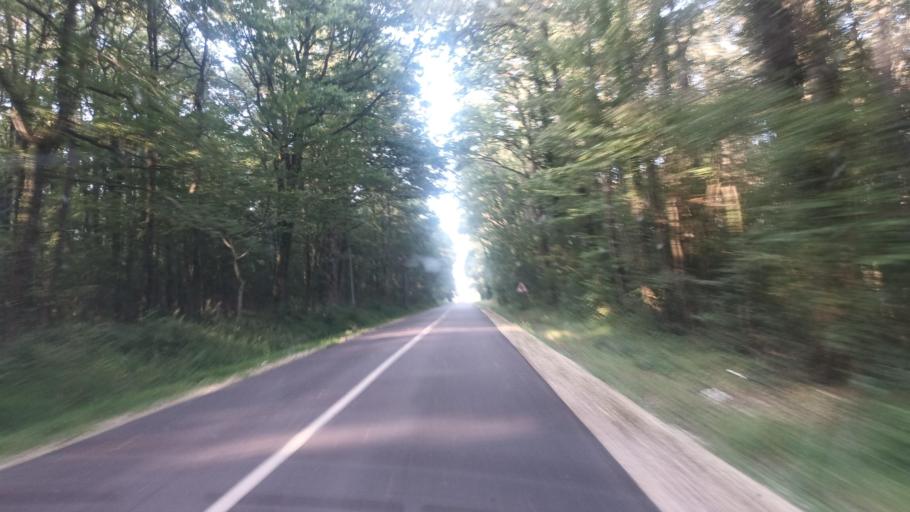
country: FR
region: Bourgogne
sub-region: Departement de l'Yonne
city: Pont-sur-Yonne
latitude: 48.2580
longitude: 3.1718
